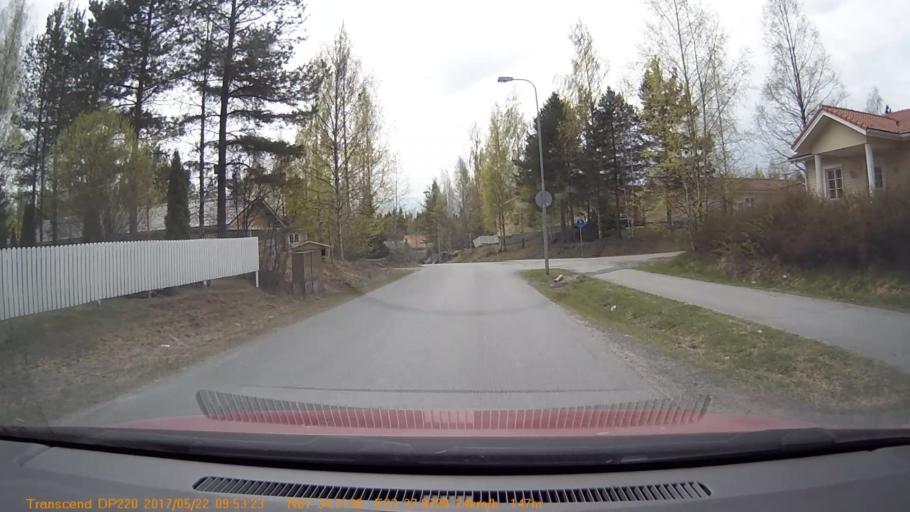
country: FI
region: Pirkanmaa
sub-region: Tampere
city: Yloejaervi
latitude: 61.5784
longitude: 23.6328
